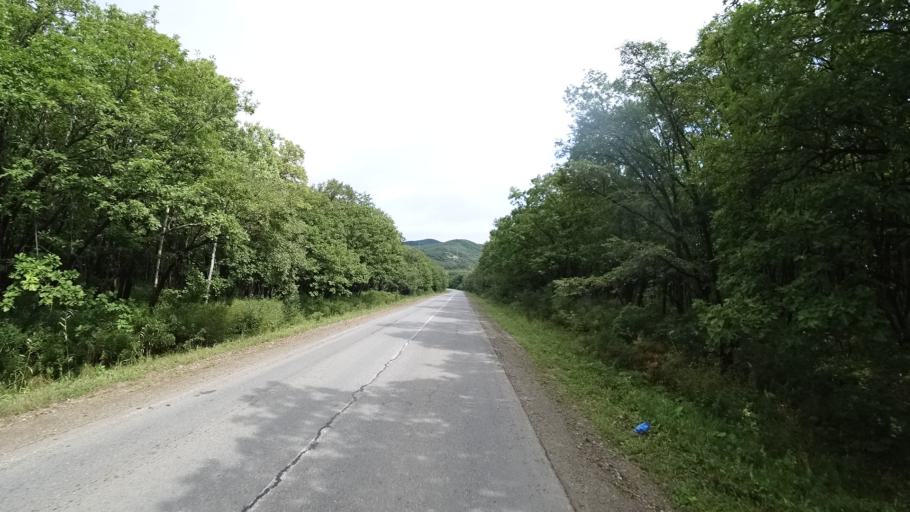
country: RU
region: Primorskiy
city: Lyalichi
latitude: 44.1395
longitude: 132.4224
